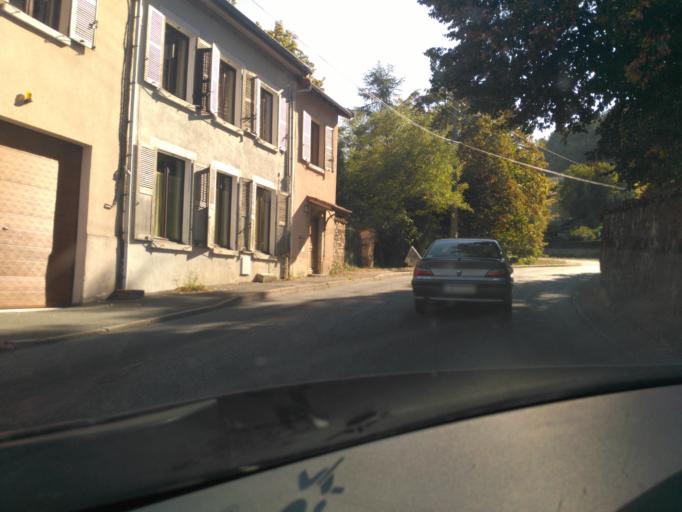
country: FR
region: Rhone-Alpes
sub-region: Departement du Rhone
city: Tarare
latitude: 45.8919
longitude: 4.4345
